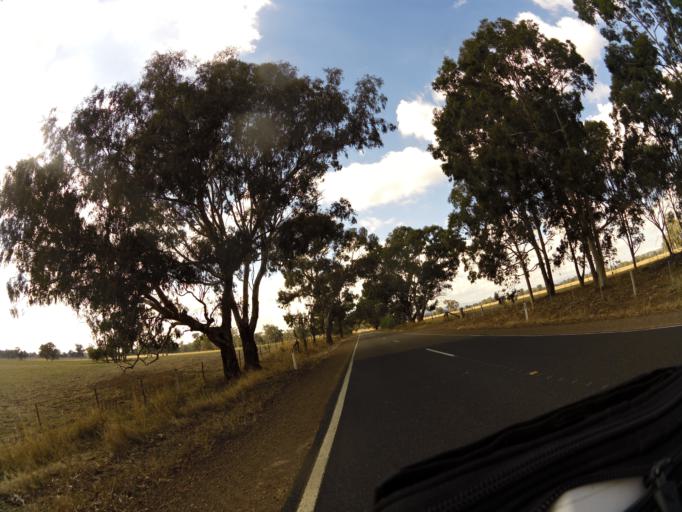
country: AU
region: Victoria
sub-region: Benalla
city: Benalla
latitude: -36.6147
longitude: 146.0261
